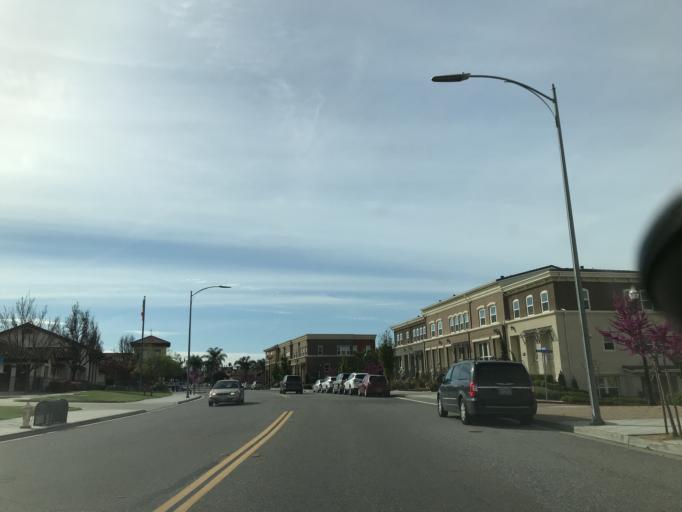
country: US
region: California
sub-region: Santa Clara County
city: Seven Trees
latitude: 37.3158
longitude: -121.7750
